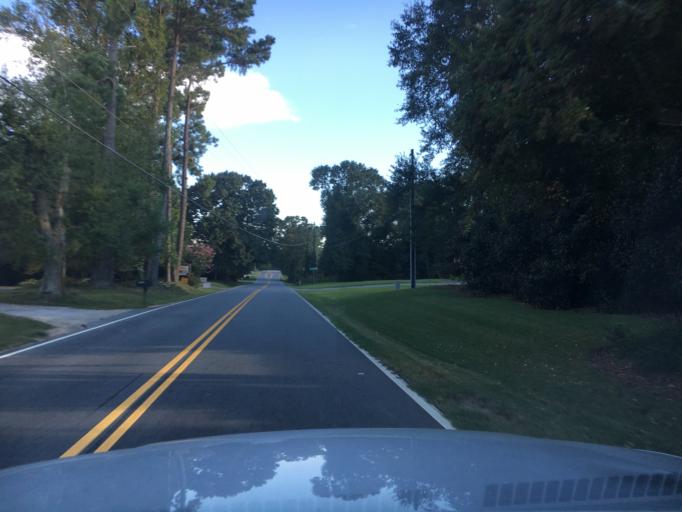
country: US
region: South Carolina
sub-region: Spartanburg County
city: Roebuck
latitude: 34.8965
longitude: -82.0073
